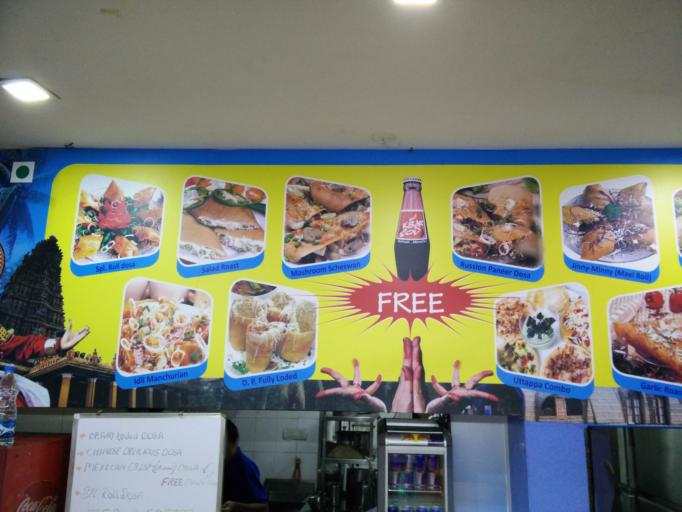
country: IN
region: Maharashtra
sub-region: Nashik Division
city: Nashik
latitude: 19.9906
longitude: 73.7613
